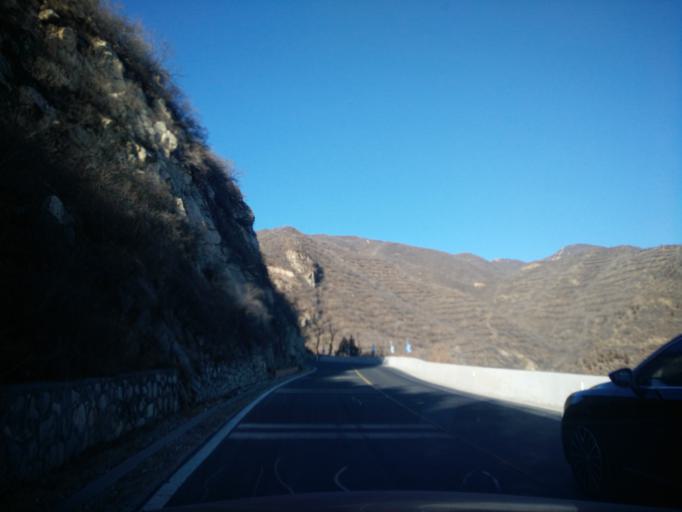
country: CN
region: Beijing
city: Wangping
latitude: 40.0073
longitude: 115.9697
